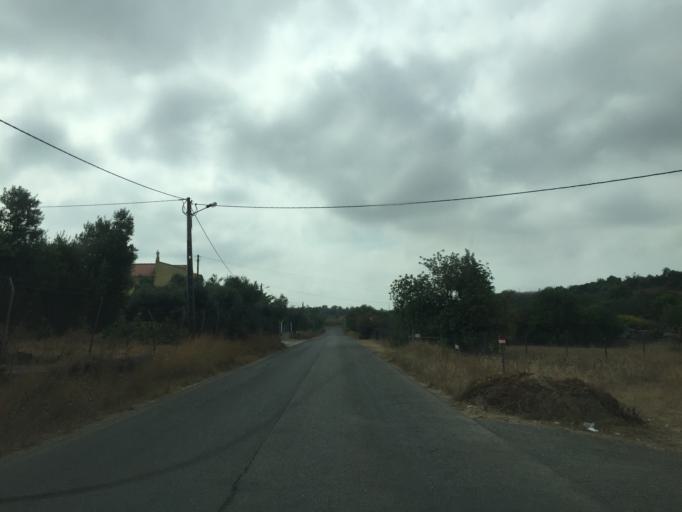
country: PT
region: Faro
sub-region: Olhao
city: Olhao
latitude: 37.0663
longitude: -7.8798
